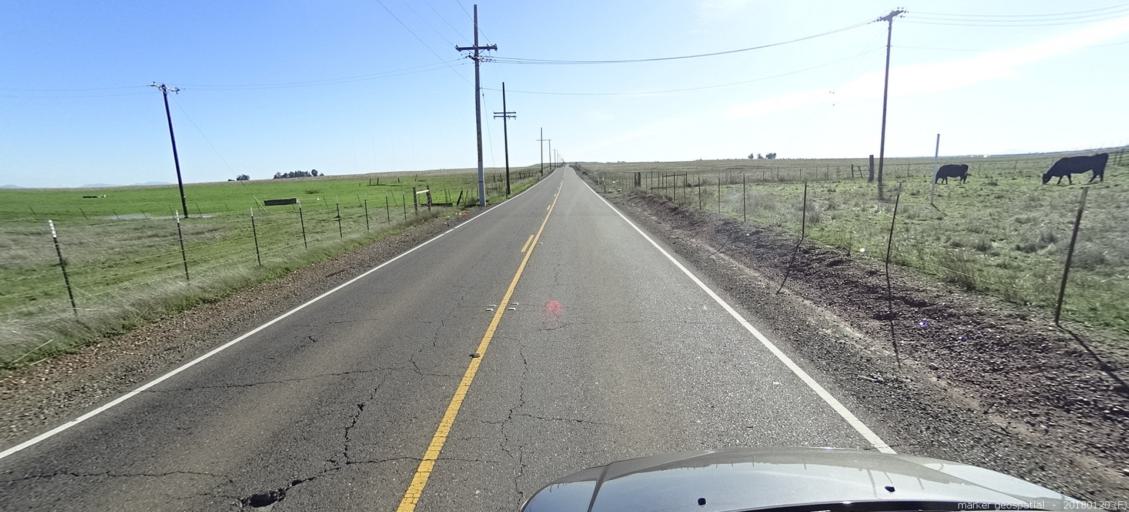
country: US
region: California
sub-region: Sacramento County
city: Gold River
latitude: 38.5692
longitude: -121.1873
